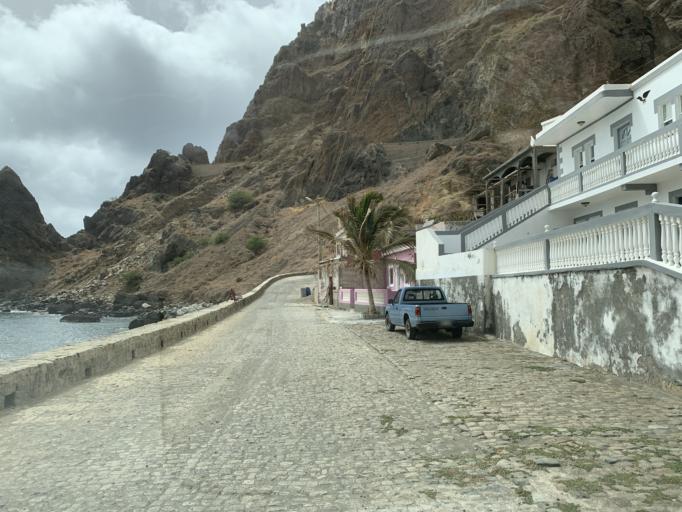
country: CV
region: Brava
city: Vila Nova Sintra
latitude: 14.8732
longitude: -24.7313
